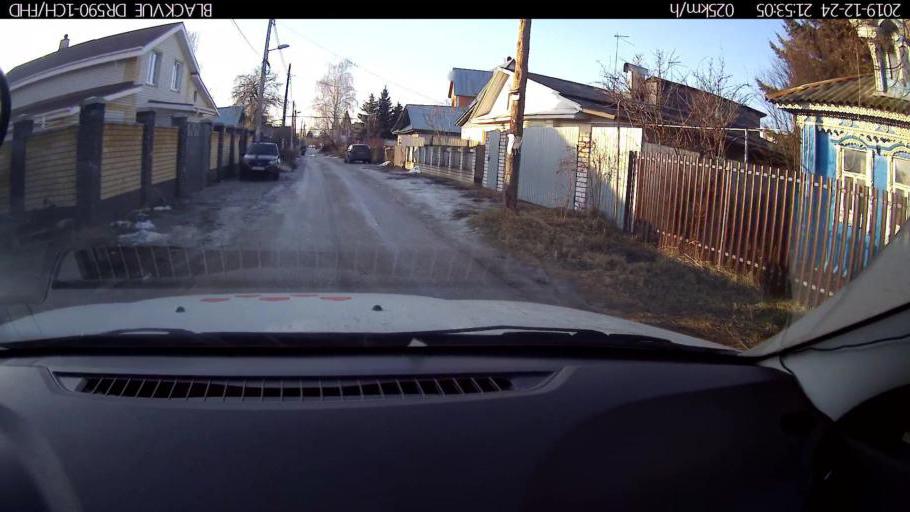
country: RU
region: Nizjnij Novgorod
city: Burevestnik
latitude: 56.2166
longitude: 43.8431
